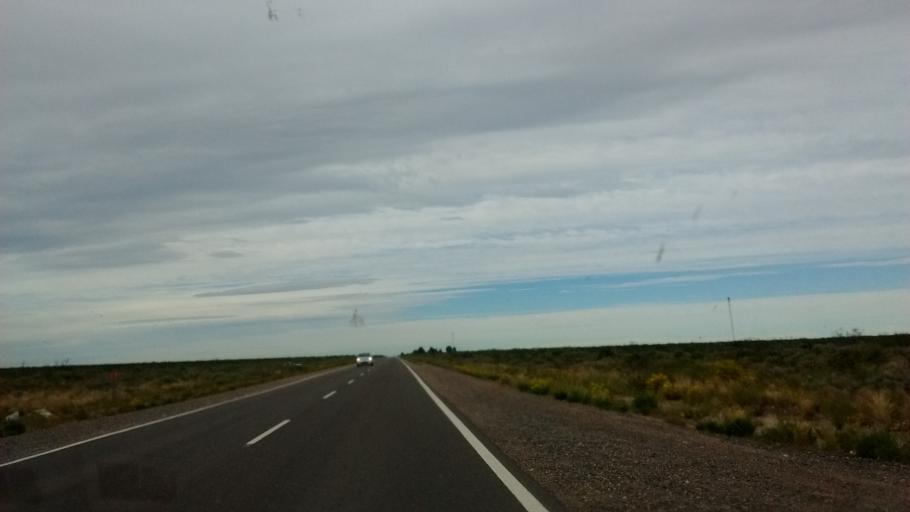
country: AR
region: Rio Negro
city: Contraalmirante Cordero
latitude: -38.3864
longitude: -68.0256
